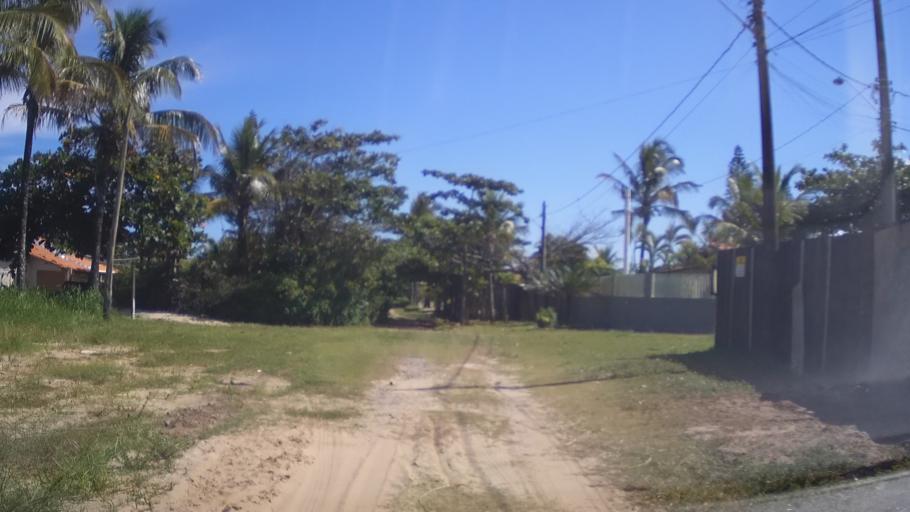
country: BR
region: Sao Paulo
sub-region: Itanhaem
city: Itanhaem
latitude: -24.1604
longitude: -46.7406
